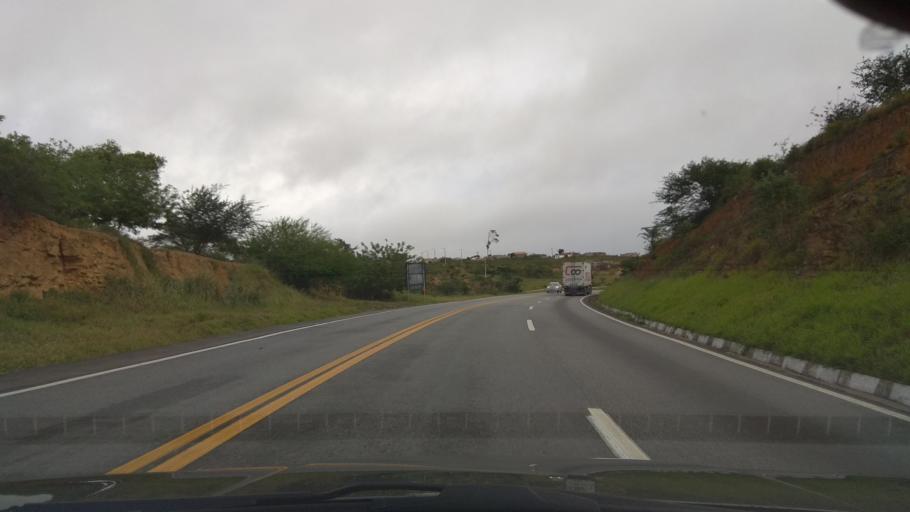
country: BR
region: Bahia
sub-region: Santa Ines
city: Santa Ines
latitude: -13.0628
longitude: -39.9571
